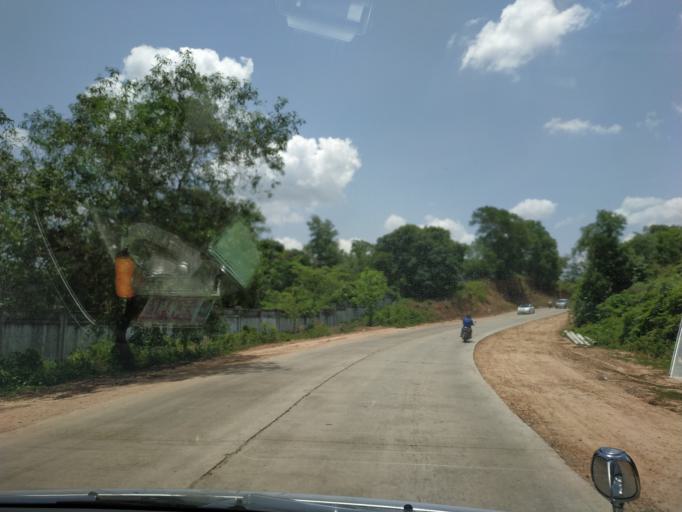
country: MM
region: Bago
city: Bago
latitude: 17.4699
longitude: 96.4640
